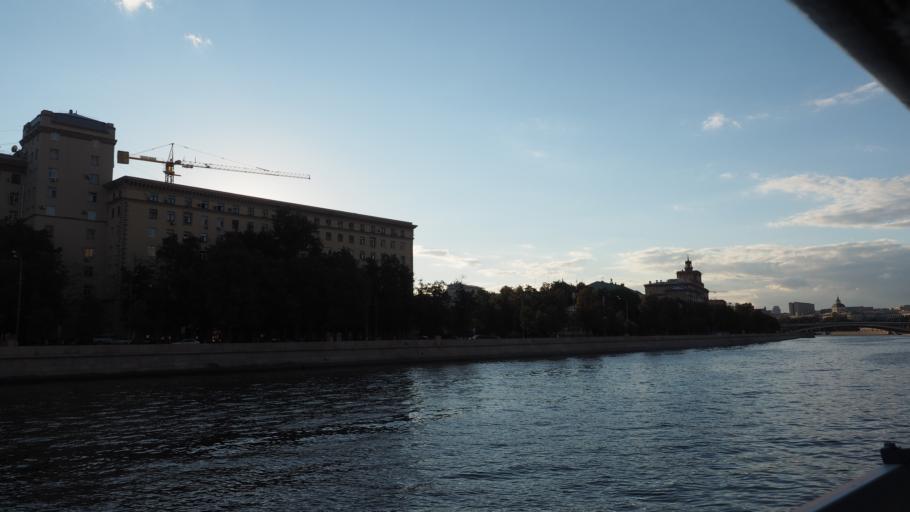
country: RU
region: Moscow
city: Zamoskvorech'ye
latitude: 55.7403
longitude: 37.6456
